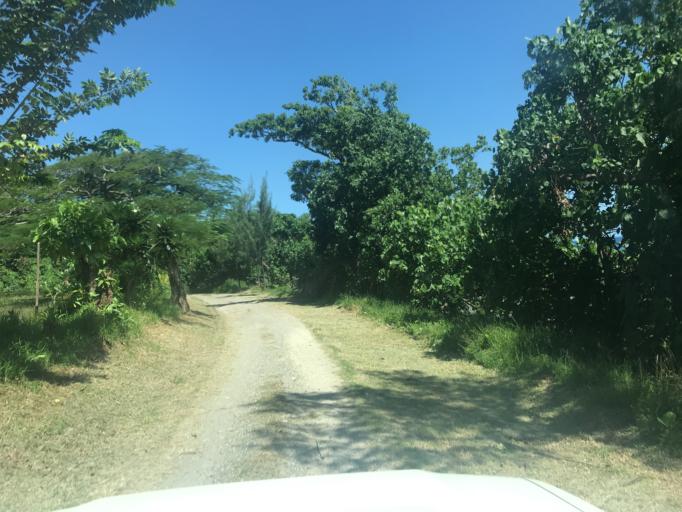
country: VU
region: Sanma
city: Luganville
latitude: -15.5965
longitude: 166.7805
